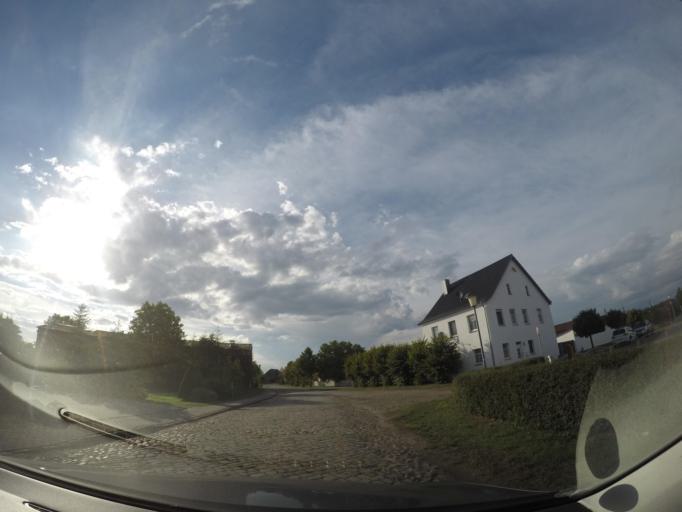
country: DE
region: Saxony-Anhalt
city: Kusey
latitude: 52.5646
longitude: 11.1334
